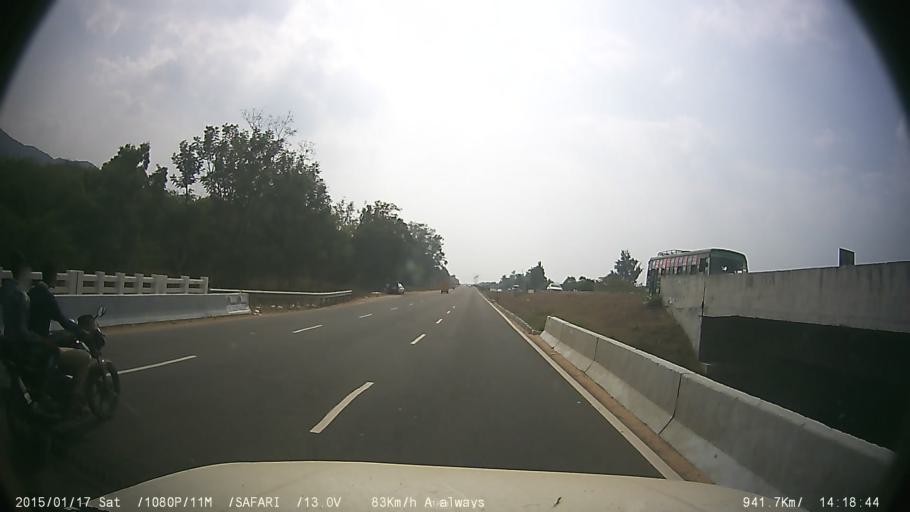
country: IN
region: Tamil Nadu
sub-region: Vellore
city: Vaniyambadi
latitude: 12.7275
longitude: 78.6732
